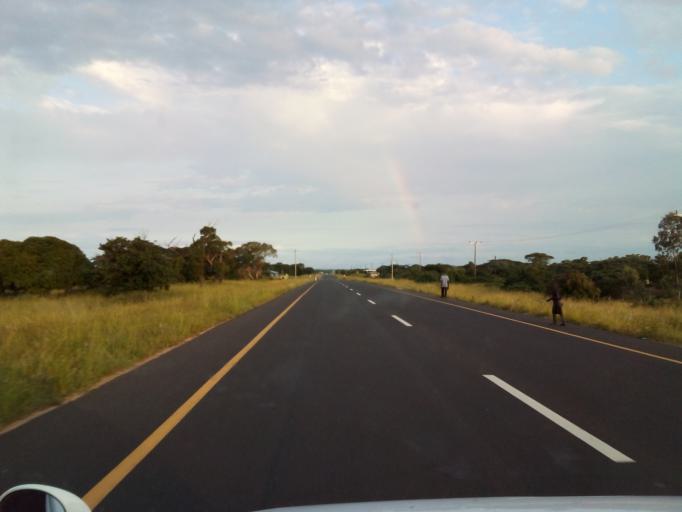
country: MZ
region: Maputo City
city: Maputo
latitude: -26.0711
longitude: 32.6081
